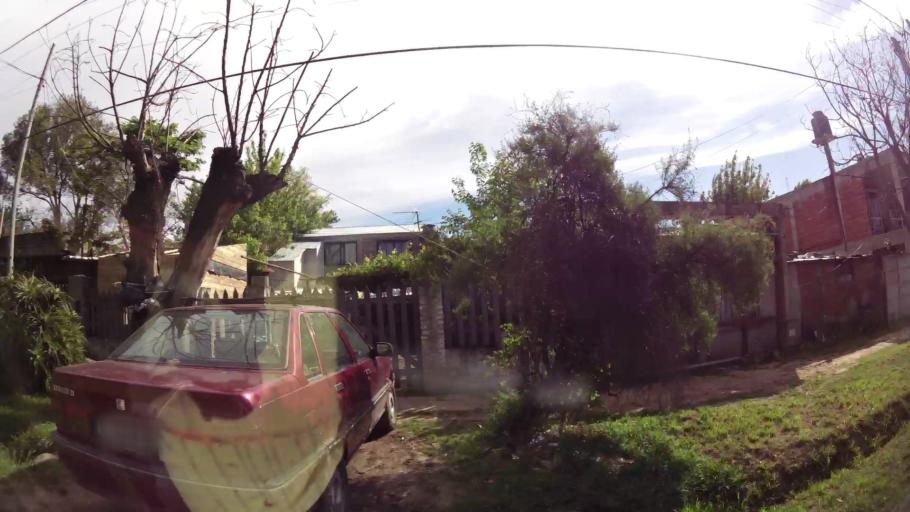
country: AR
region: Buenos Aires
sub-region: Partido de Almirante Brown
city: Adrogue
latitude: -34.8109
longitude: -58.3529
